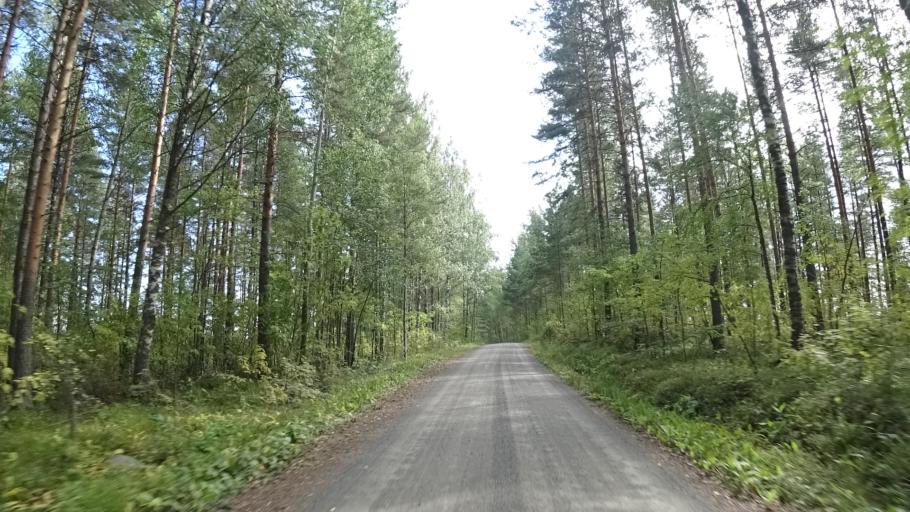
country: FI
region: North Karelia
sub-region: Keski-Karjala
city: Raeaekkylae
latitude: 62.3932
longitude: 29.7714
